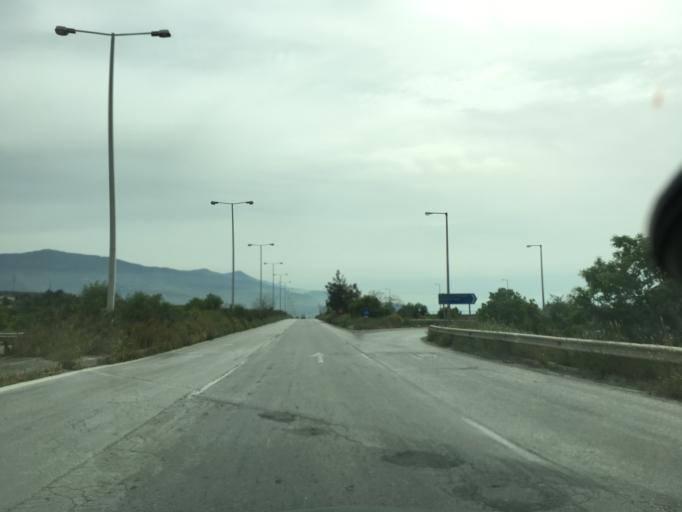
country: GR
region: Thessaly
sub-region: Nomos Magnisias
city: Nea Ionia
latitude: 39.3778
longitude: 22.8816
